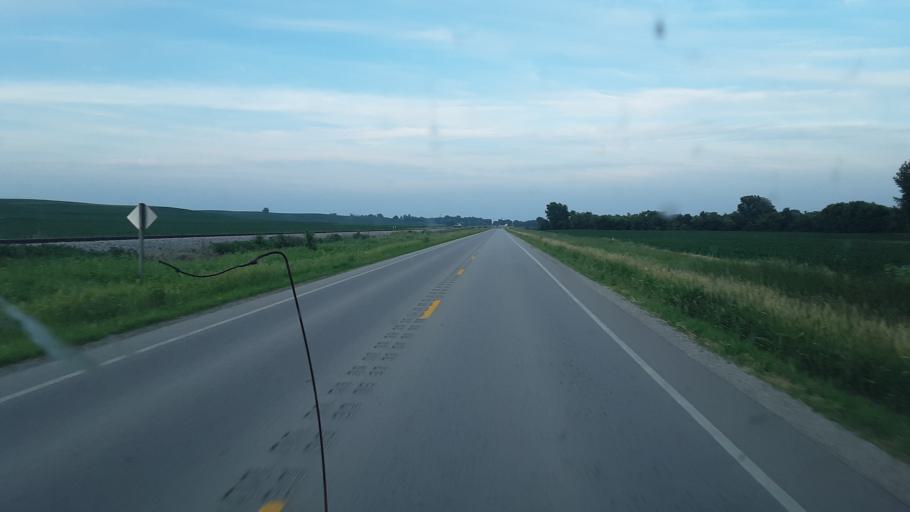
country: US
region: Iowa
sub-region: Iowa County
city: Marengo
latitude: 41.7478
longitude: -92.2179
